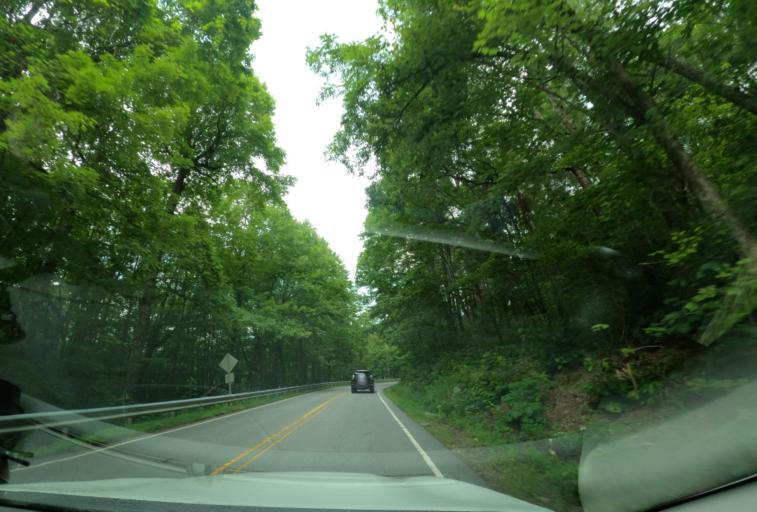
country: US
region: North Carolina
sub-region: Jackson County
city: Cullowhee
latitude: 35.1090
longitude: -83.1450
